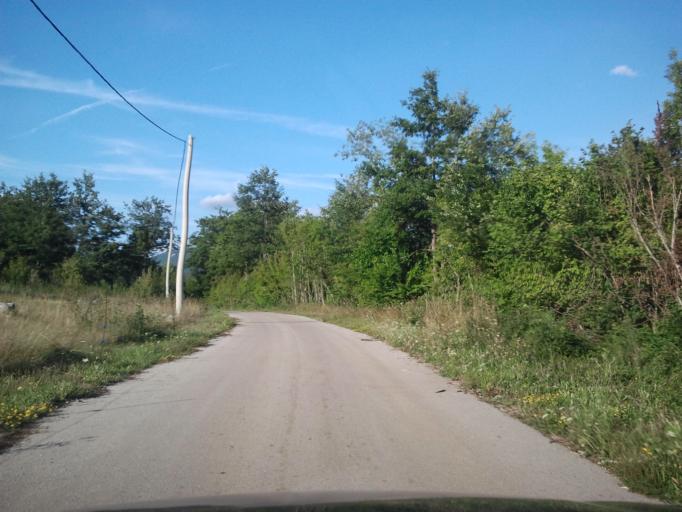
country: HR
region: Zadarska
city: Gracac
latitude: 44.3744
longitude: 15.7067
